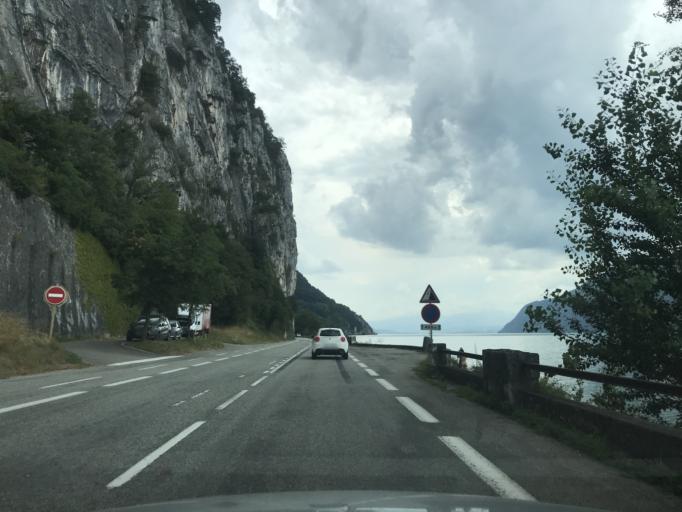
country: FR
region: Rhone-Alpes
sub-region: Departement de la Savoie
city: Chatillon
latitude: 45.7734
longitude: 5.8675
